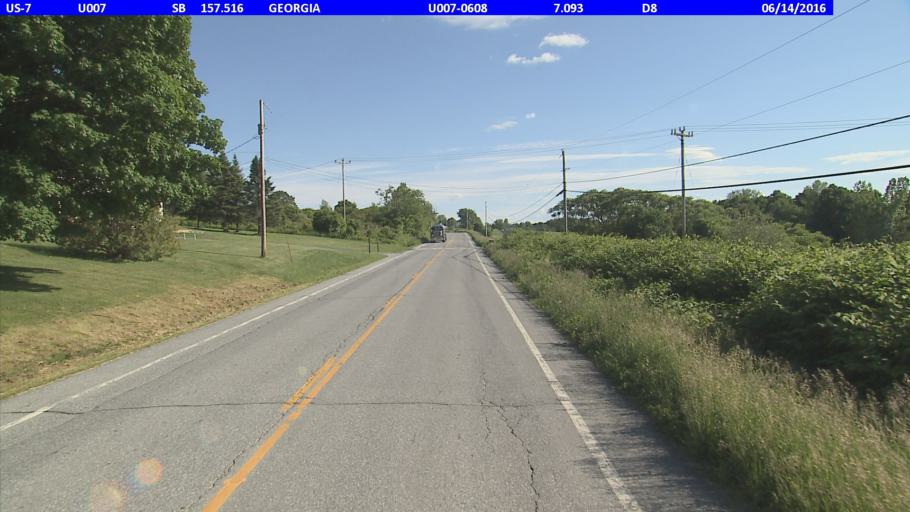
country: US
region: Vermont
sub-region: Franklin County
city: Saint Albans
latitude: 44.7731
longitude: -73.1072
